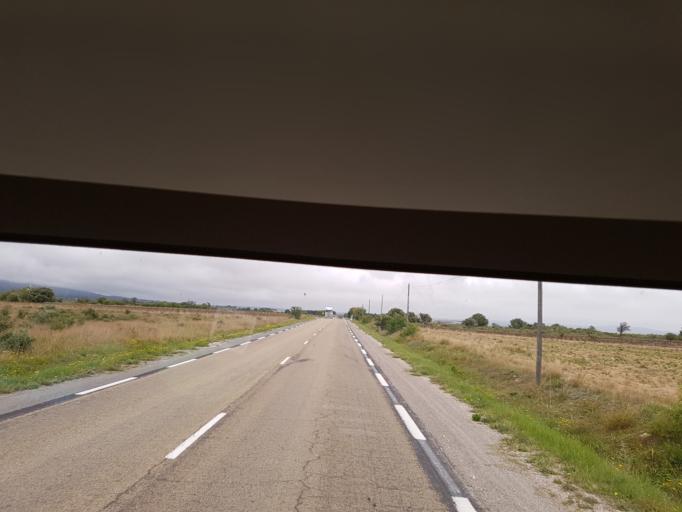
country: FR
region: Languedoc-Roussillon
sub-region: Departement de l'Aude
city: Leucate
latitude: 42.9228
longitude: 2.9953
